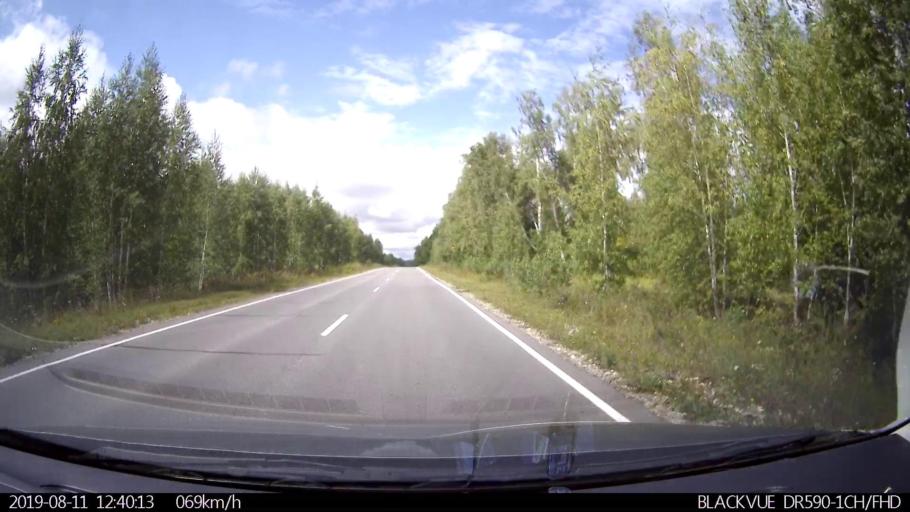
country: RU
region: Ulyanovsk
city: Ignatovka
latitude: 53.8374
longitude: 47.7842
